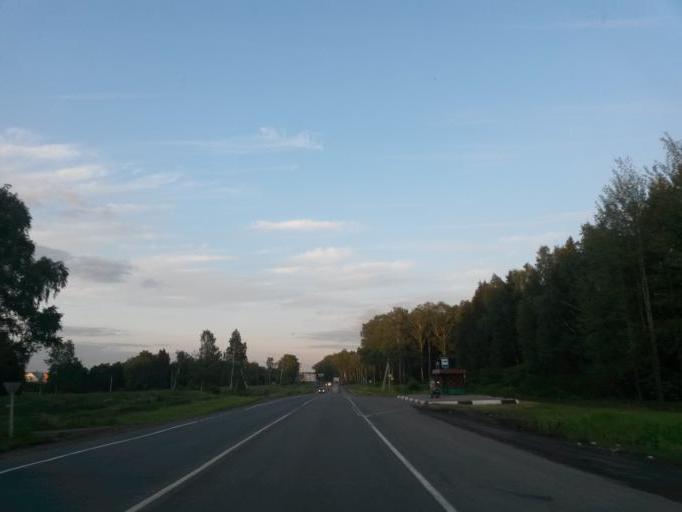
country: RU
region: Moskovskaya
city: L'vovskiy
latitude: 55.3315
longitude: 37.5780
